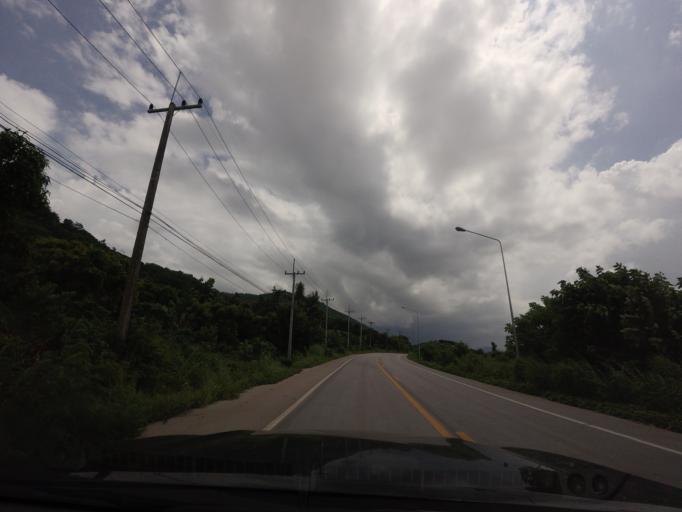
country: TH
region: Loei
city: Pak Chom
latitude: 18.0275
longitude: 101.7659
